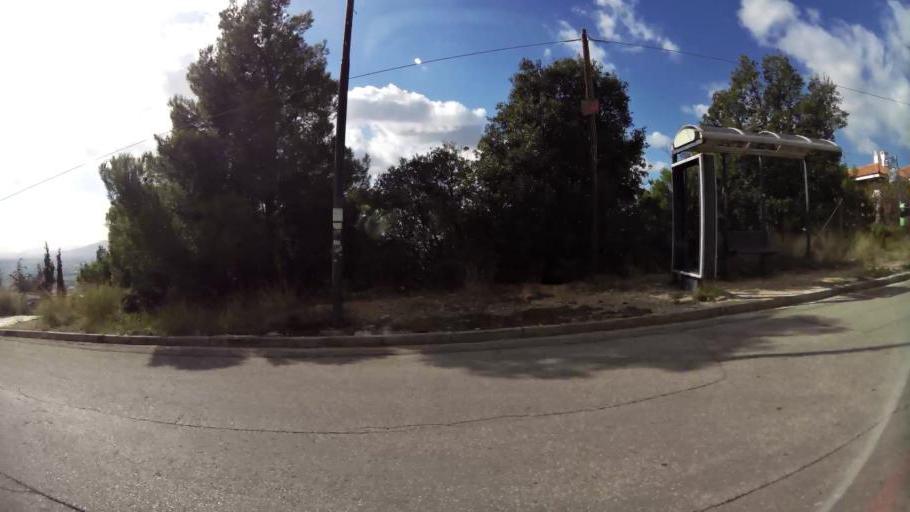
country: GR
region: Attica
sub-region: Nomarchia Anatolikis Attikis
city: Thrakomakedones
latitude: 38.1424
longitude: 23.7480
